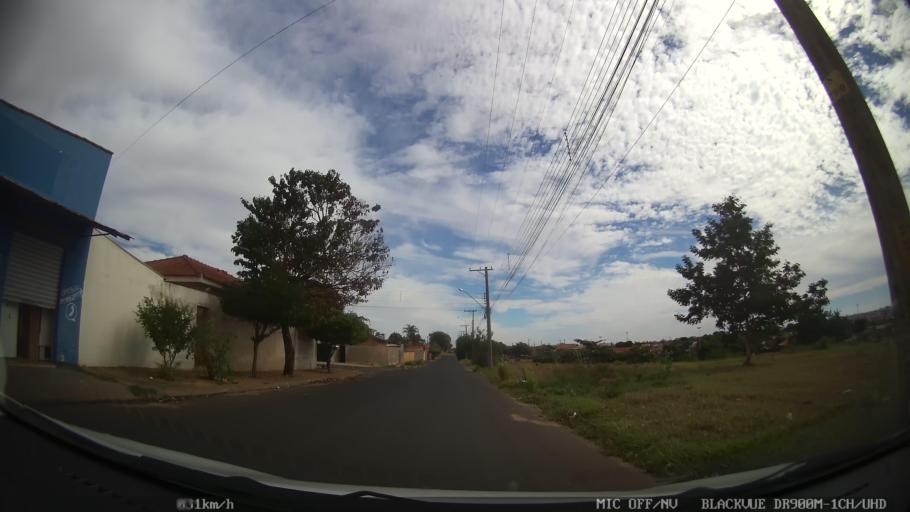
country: BR
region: Sao Paulo
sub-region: Catanduva
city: Catanduva
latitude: -21.1623
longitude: -48.9685
